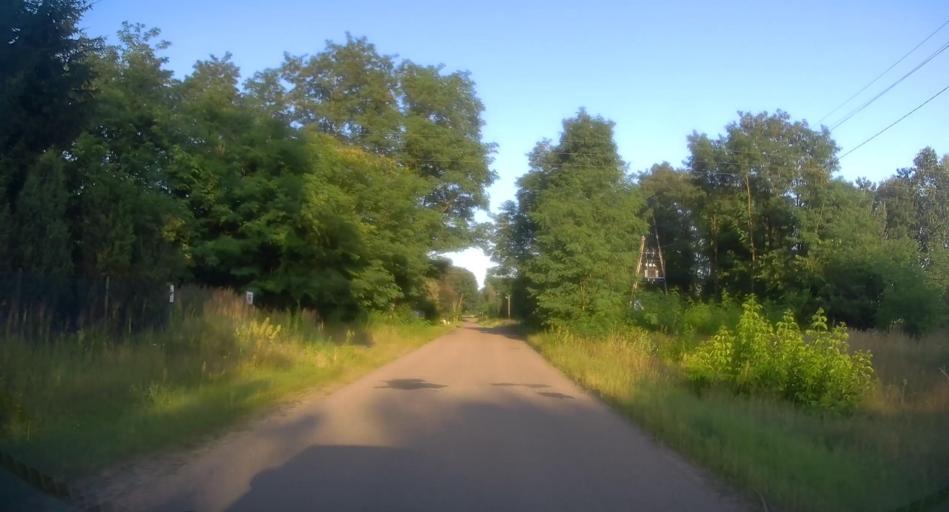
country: PL
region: Lodz Voivodeship
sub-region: Powiat skierniewicki
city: Kowiesy
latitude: 51.9034
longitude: 20.3604
